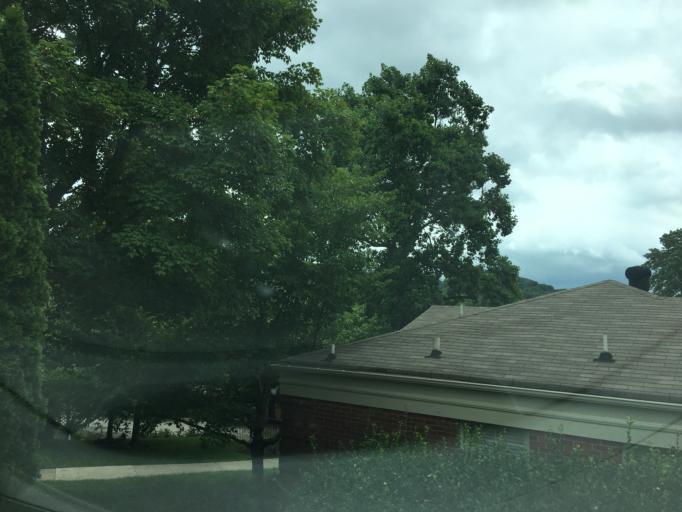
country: US
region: Tennessee
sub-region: Davidson County
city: Belle Meade
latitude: 36.0929
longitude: -86.8287
